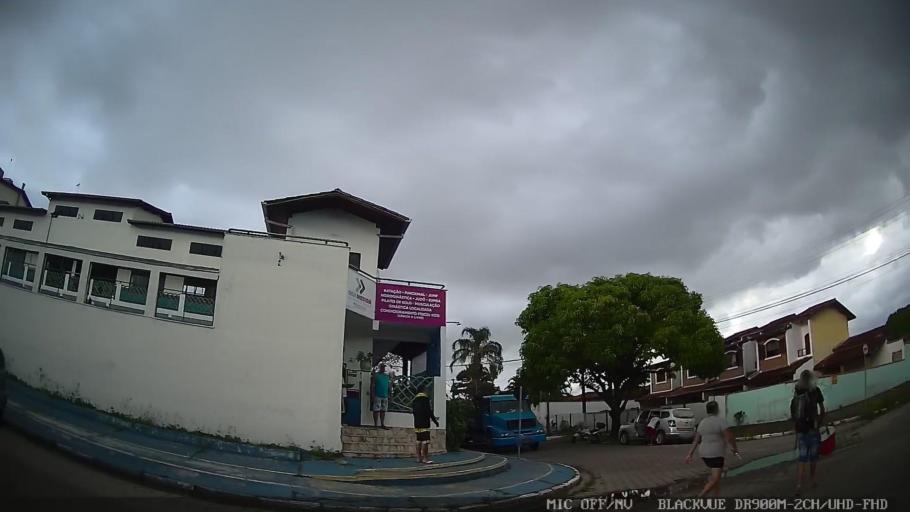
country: BR
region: Sao Paulo
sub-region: Caraguatatuba
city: Caraguatatuba
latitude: -23.6311
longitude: -45.4192
